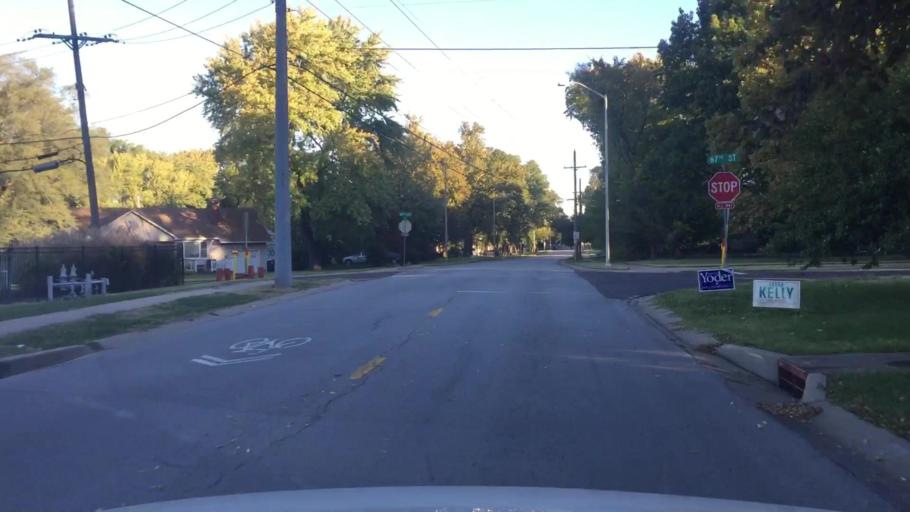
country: US
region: Kansas
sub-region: Johnson County
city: Overland Park
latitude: 39.0075
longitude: -94.6722
